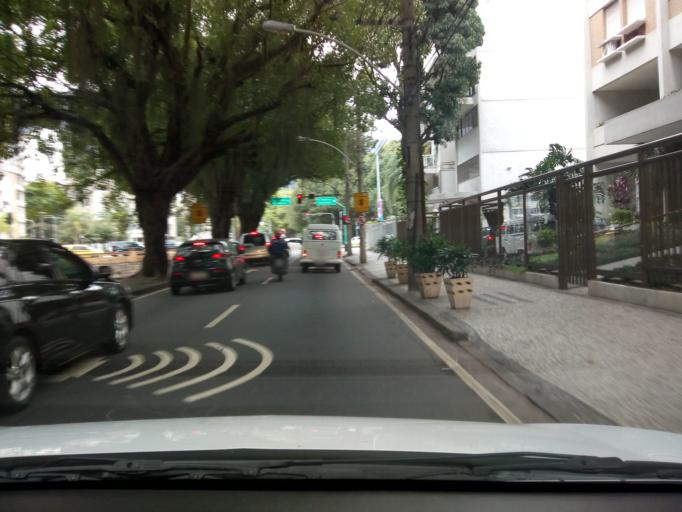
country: BR
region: Rio de Janeiro
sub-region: Rio De Janeiro
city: Rio de Janeiro
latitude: -22.9792
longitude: -43.2264
